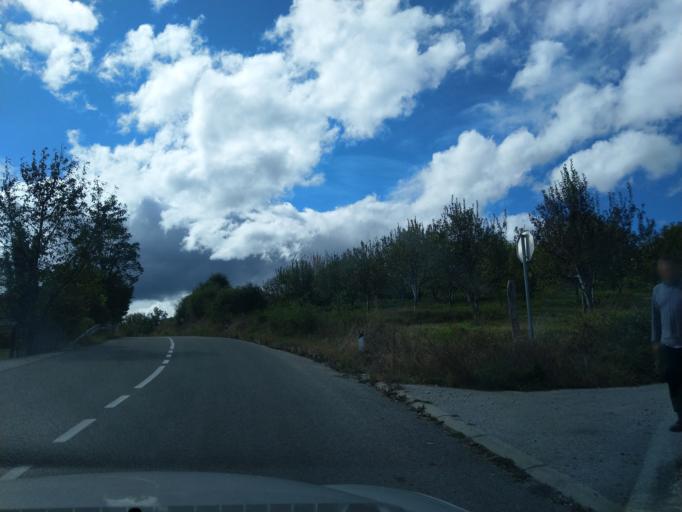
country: RS
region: Central Serbia
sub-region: Zlatiborski Okrug
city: Cajetina
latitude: 43.7248
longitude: 19.8049
